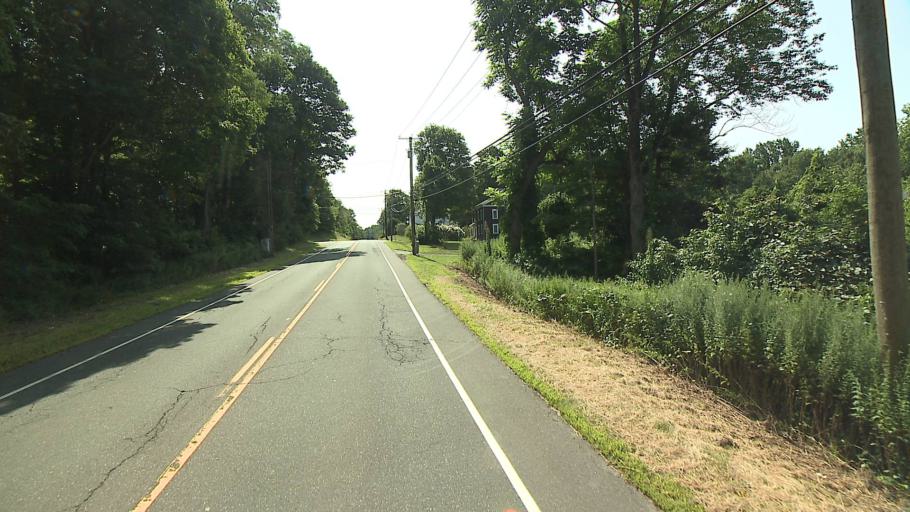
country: US
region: Connecticut
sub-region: Fairfield County
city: Trumbull
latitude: 41.2605
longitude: -73.2883
